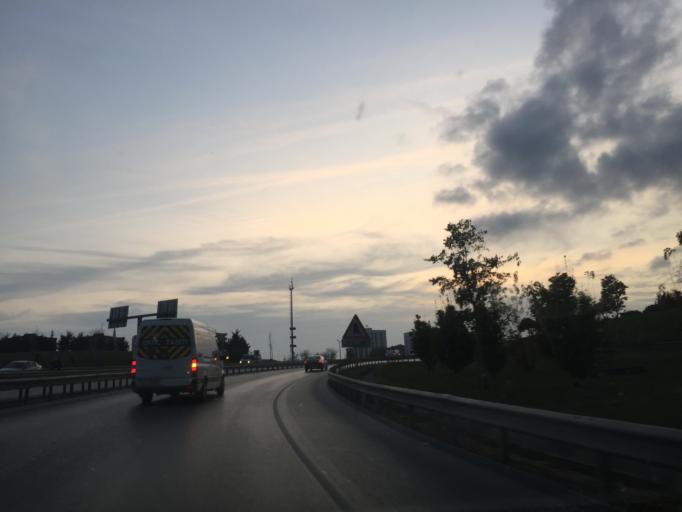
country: TR
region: Istanbul
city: Samandira
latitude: 40.9699
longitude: 29.2194
